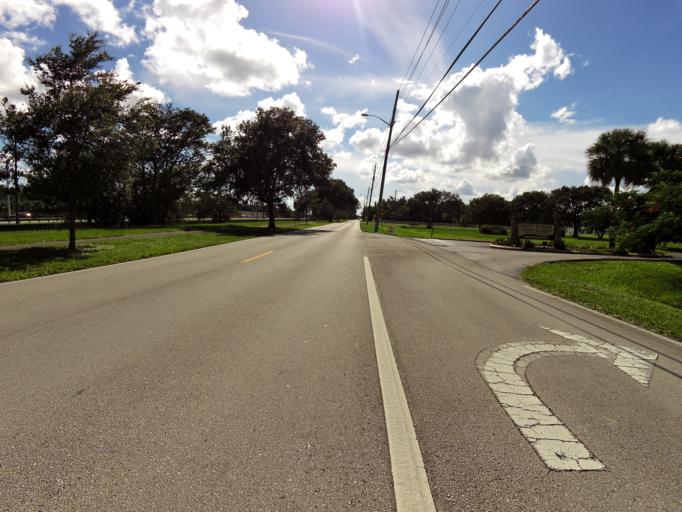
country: US
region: Florida
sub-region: Broward County
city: Cooper City
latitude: 26.0650
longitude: -80.2690
